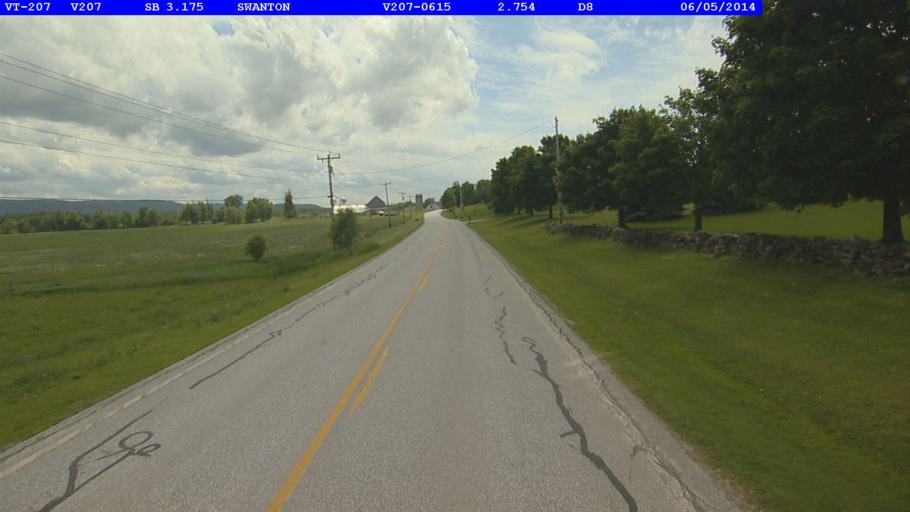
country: US
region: Vermont
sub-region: Franklin County
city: Swanton
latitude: 44.8839
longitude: -73.0681
